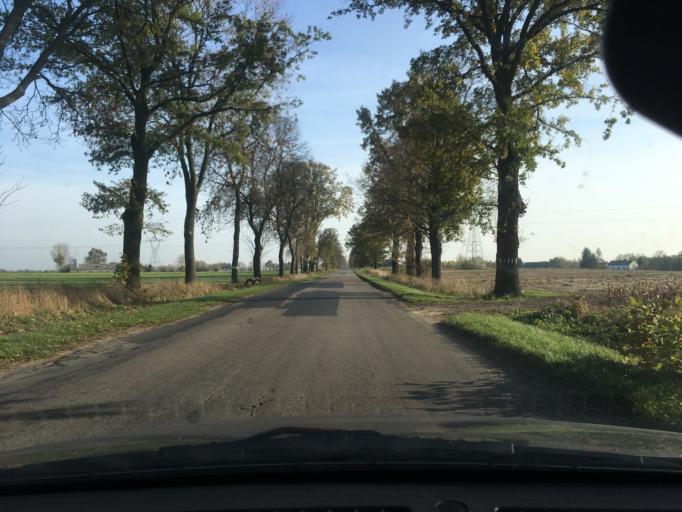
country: PL
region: Masovian Voivodeship
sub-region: Powiat plocki
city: Bodzanow
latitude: 52.4854
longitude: 20.0582
